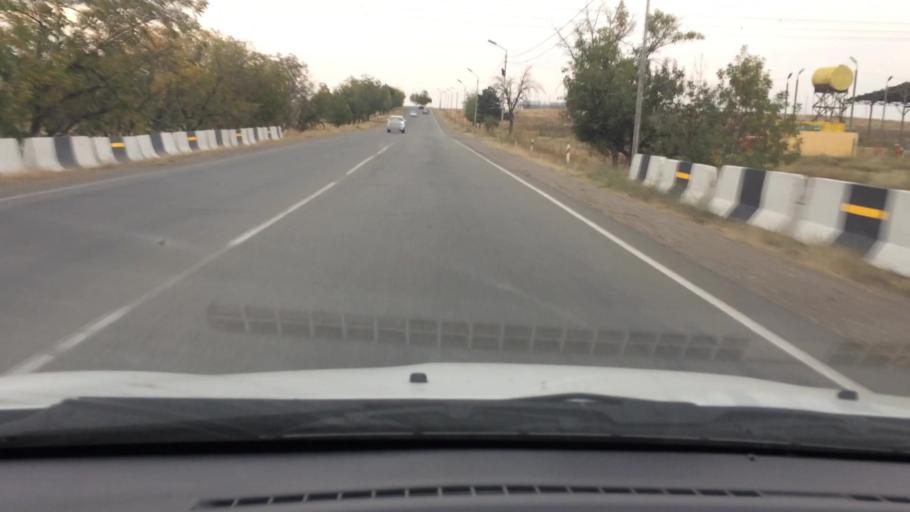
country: GE
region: Kvemo Kartli
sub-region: Marneuli
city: Marneuli
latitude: 41.5198
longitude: 44.7810
